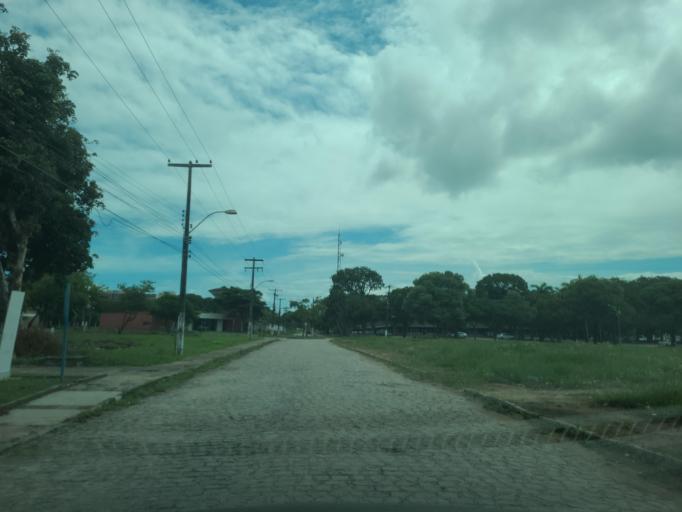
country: BR
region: Alagoas
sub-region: Satuba
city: Satuba
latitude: -9.5566
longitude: -35.7767
